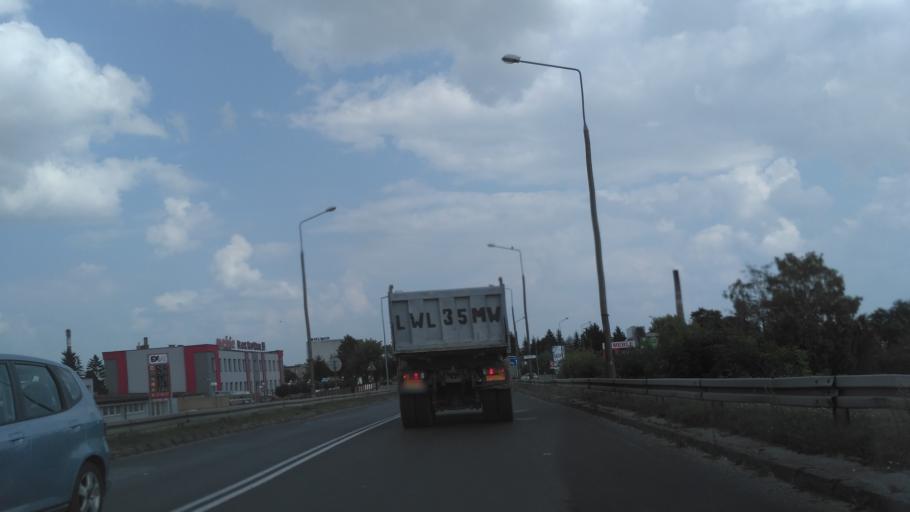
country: PL
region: Lublin Voivodeship
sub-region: Chelm
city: Chelm
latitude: 51.1448
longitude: 23.4801
